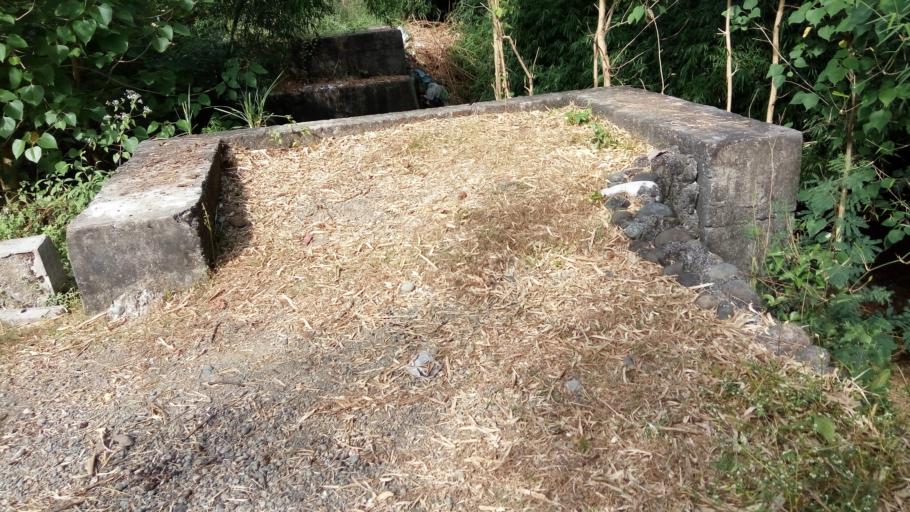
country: PH
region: Ilocos
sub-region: Province of La Union
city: Aringay
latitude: 16.3781
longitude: 120.3521
